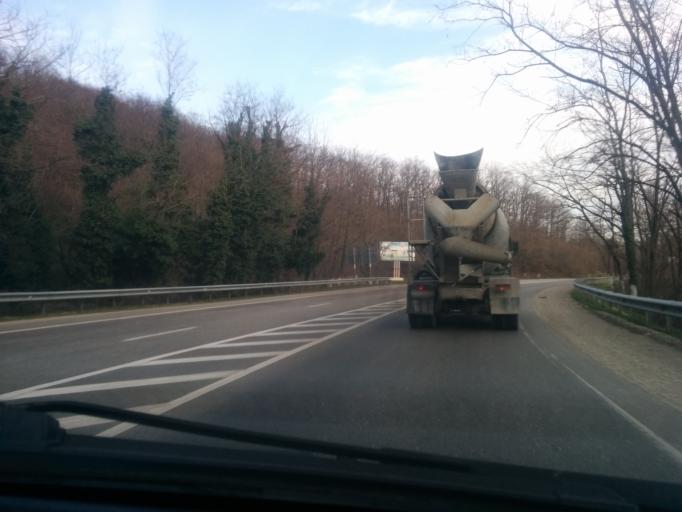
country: RU
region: Krasnodarskiy
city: Nebug
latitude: 44.1772
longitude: 38.9527
